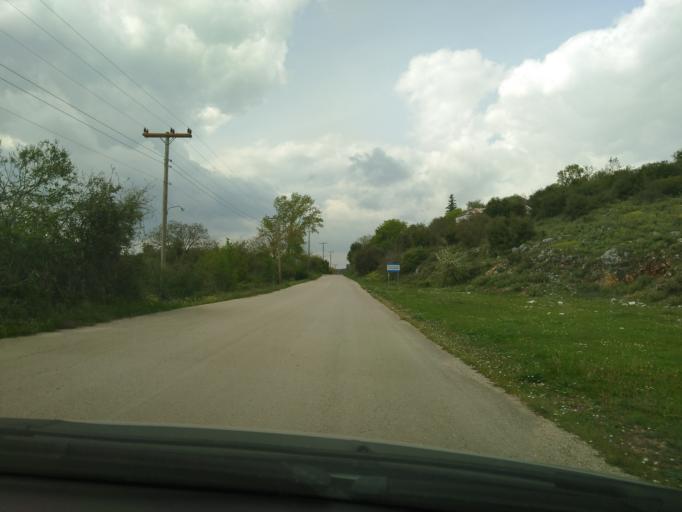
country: GR
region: Epirus
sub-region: Nomos Ioanninon
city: Asprangeloi
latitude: 39.7758
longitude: 20.6890
